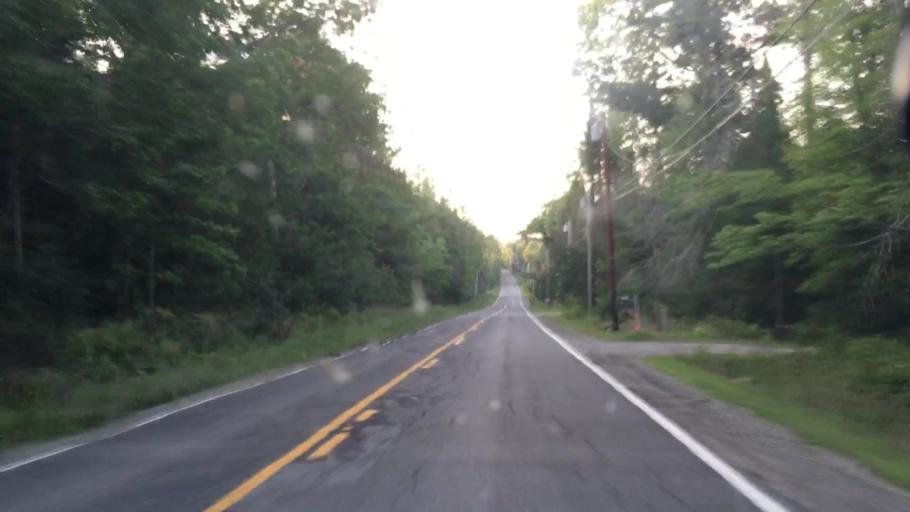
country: US
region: Maine
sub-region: Penobscot County
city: Hermon
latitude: 44.7020
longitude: -68.9465
